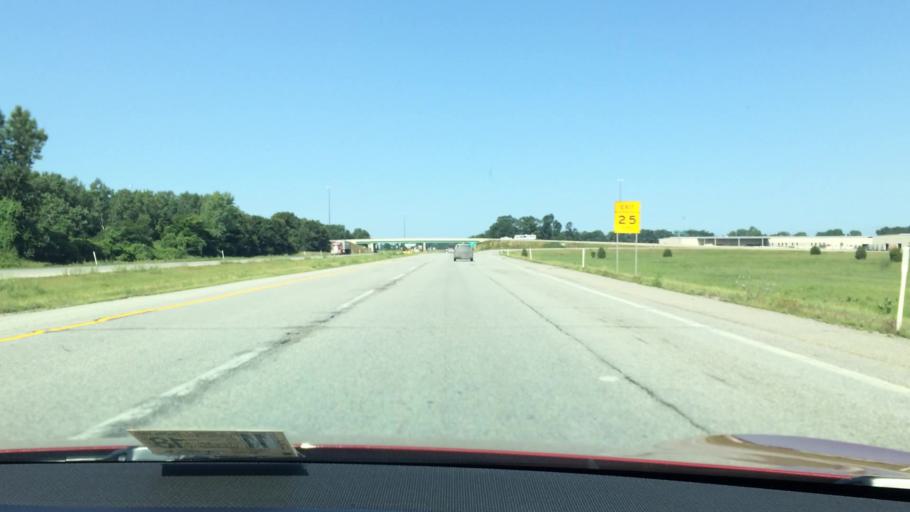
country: US
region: Michigan
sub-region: Saint Joseph County
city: White Pigeon
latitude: 41.7473
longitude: -85.6811
